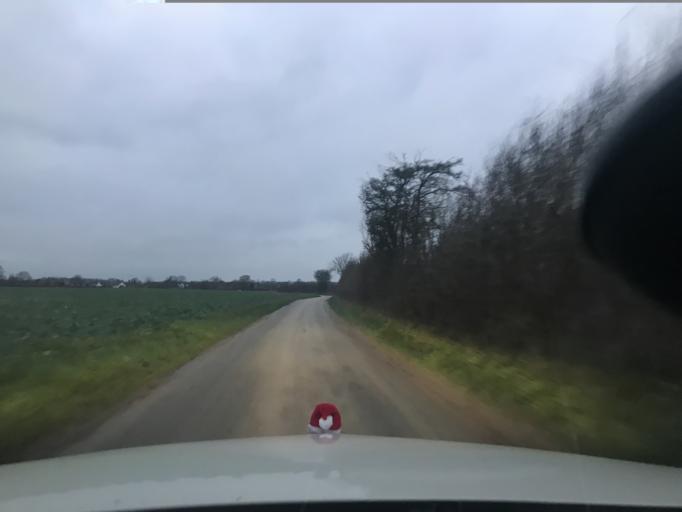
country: DK
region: South Denmark
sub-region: Sonderborg Kommune
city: Dybbol
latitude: 54.8556
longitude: 9.7305
